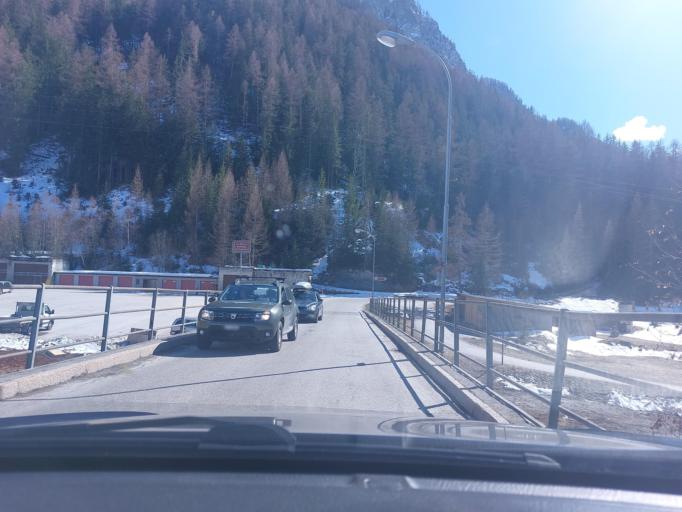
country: CH
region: Valais
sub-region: Herens District
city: Evolene
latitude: 46.0810
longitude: 7.5084
